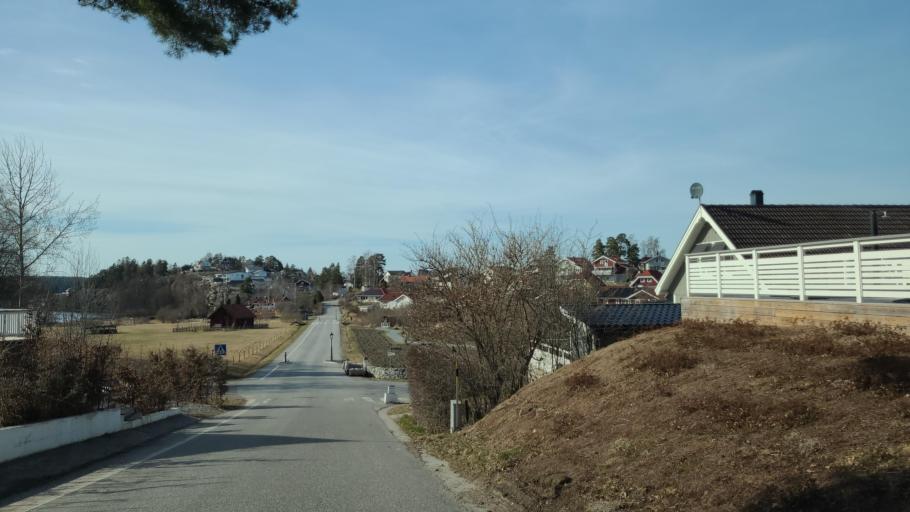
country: SE
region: Stockholm
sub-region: Ekero Kommun
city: Ekeroe
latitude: 59.2861
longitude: 17.7700
